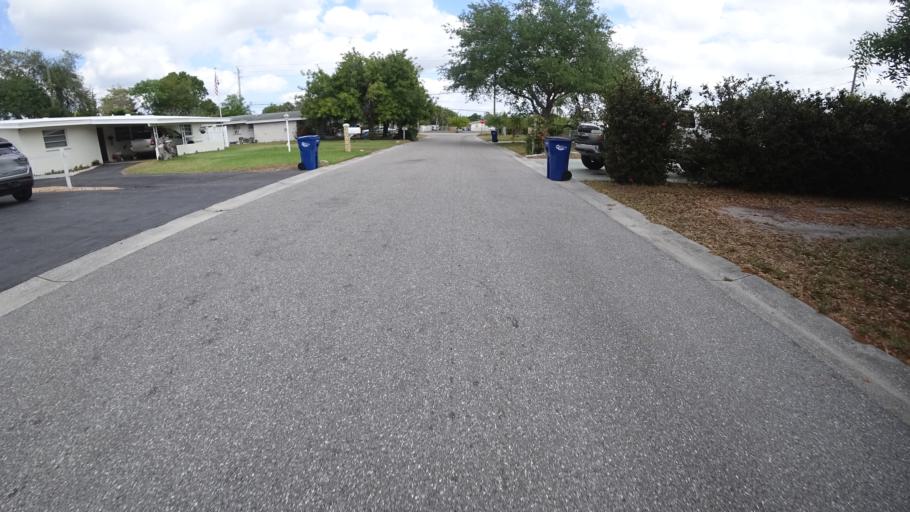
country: US
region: Florida
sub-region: Manatee County
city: Bayshore Gardens
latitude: 27.4397
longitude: -82.5845
